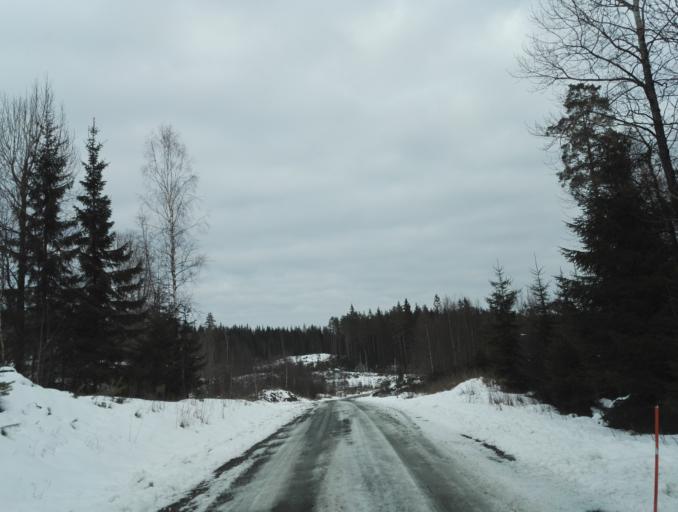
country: SE
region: Vaestra Goetaland
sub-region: Bollebygds Kommun
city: Bollebygd
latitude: 57.7709
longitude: 12.5925
